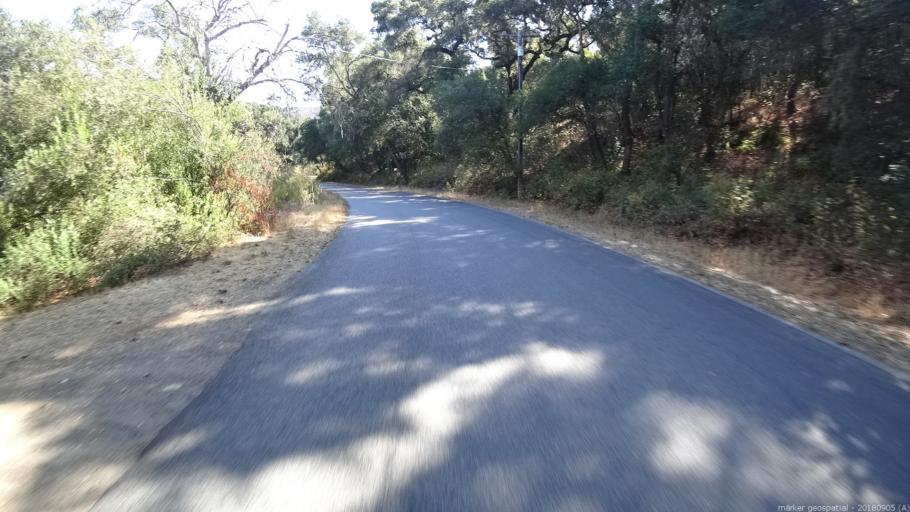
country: US
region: California
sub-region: Monterey County
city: Carmel Valley Village
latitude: 36.3930
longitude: -121.6123
